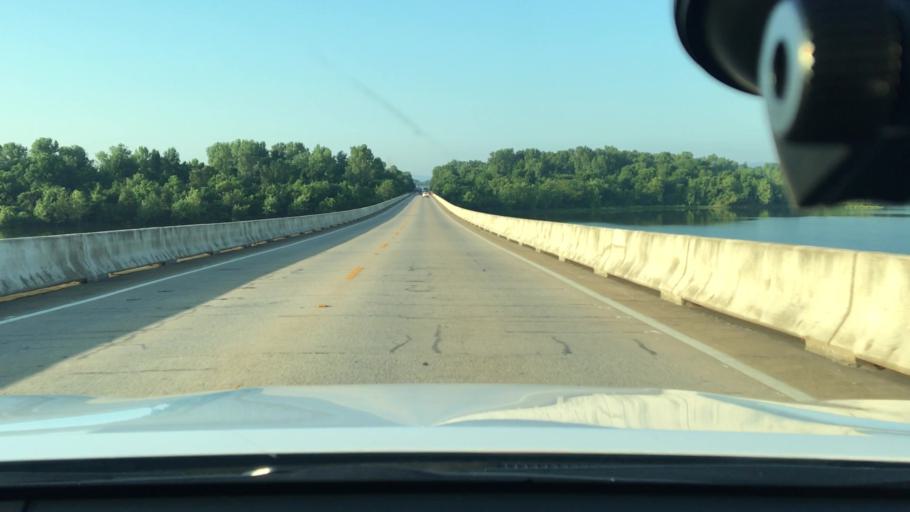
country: US
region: Arkansas
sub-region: Johnson County
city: Clarksville
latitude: 35.4079
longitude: -93.5318
